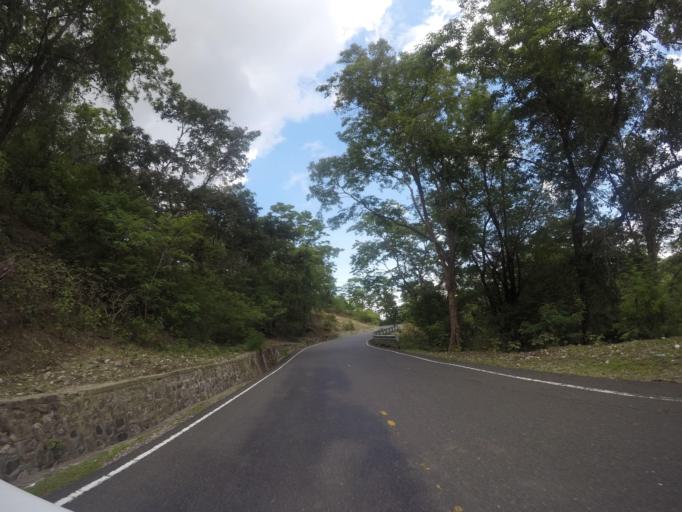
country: TL
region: Bobonaro
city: Maliana
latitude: -8.9525
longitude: 125.0892
